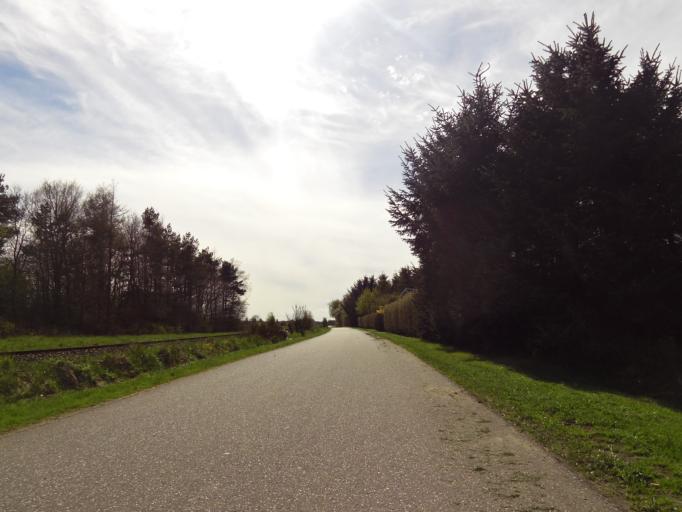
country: DK
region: Central Jutland
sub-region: Skive Kommune
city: Skive
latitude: 56.5578
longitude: 8.9669
